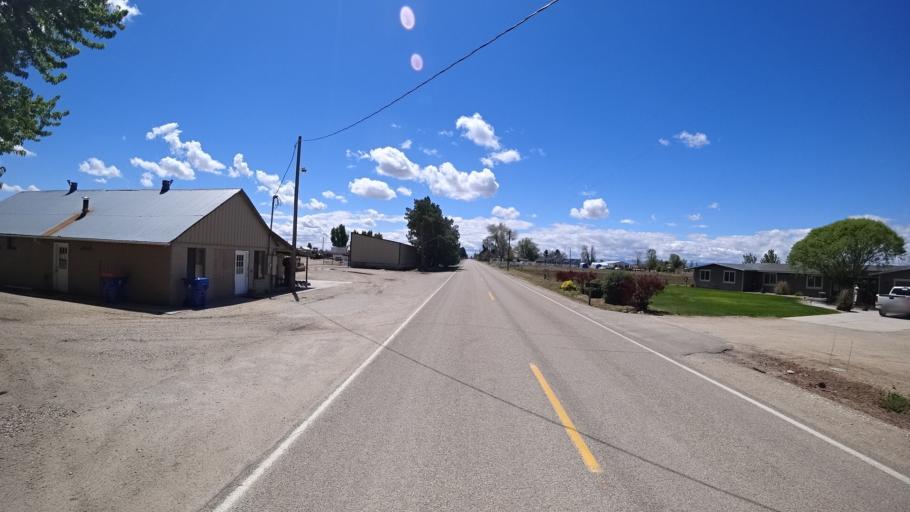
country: US
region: Idaho
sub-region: Ada County
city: Kuna
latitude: 43.4771
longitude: -116.3544
